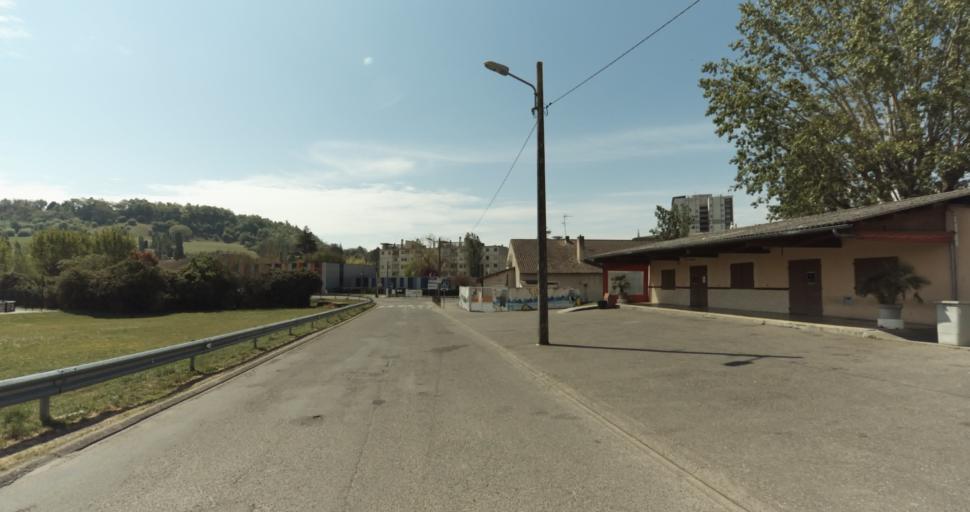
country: FR
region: Aquitaine
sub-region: Departement du Lot-et-Garonne
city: Agen
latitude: 44.2153
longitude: 0.6494
